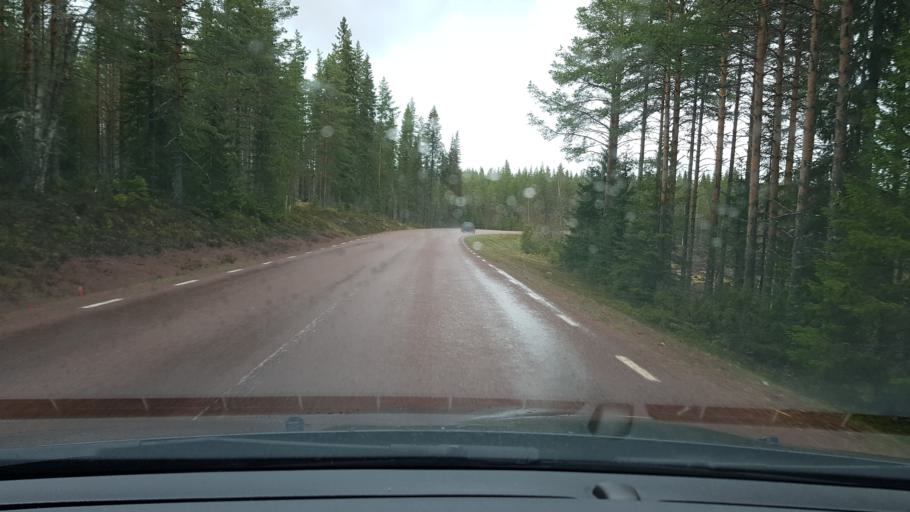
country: SE
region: Dalarna
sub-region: Malung-Saelens kommun
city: Malung
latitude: 61.0597
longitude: 13.4583
